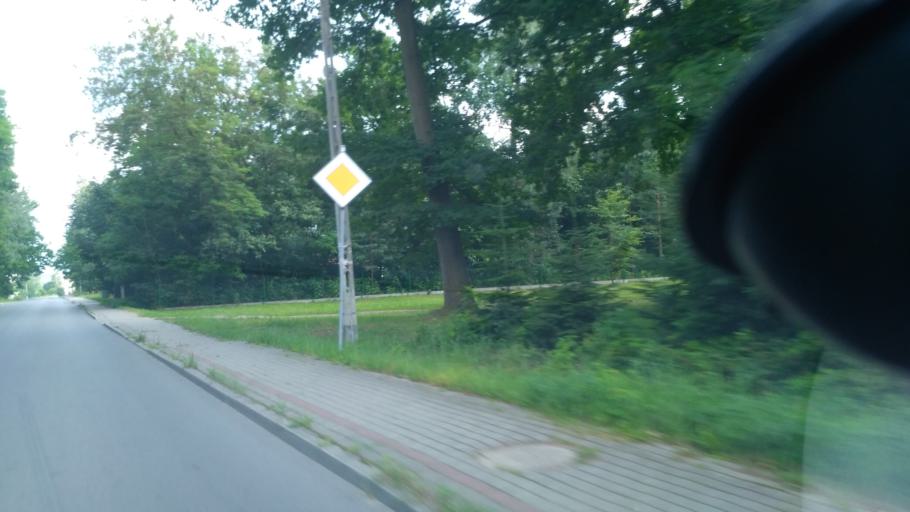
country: PL
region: Subcarpathian Voivodeship
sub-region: Powiat rzeszowski
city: Wysoka Glogowska
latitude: 50.1306
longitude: 22.0239
